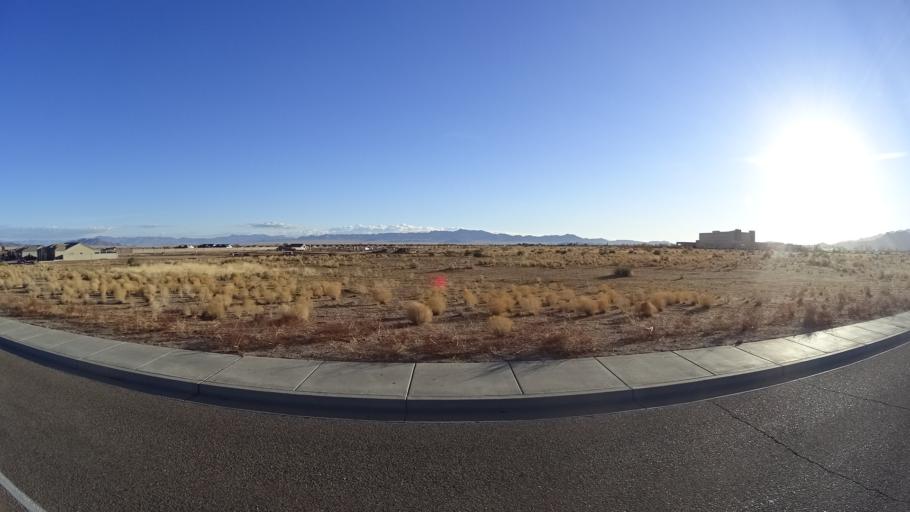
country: US
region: Arizona
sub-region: Mohave County
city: New Kingman-Butler
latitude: 35.2198
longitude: -113.9911
